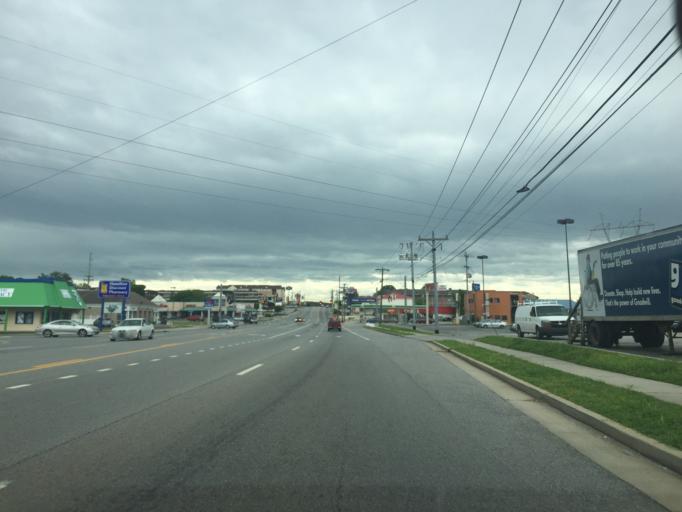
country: US
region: Tennessee
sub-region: Hamilton County
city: East Brainerd
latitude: 35.0455
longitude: -85.1642
